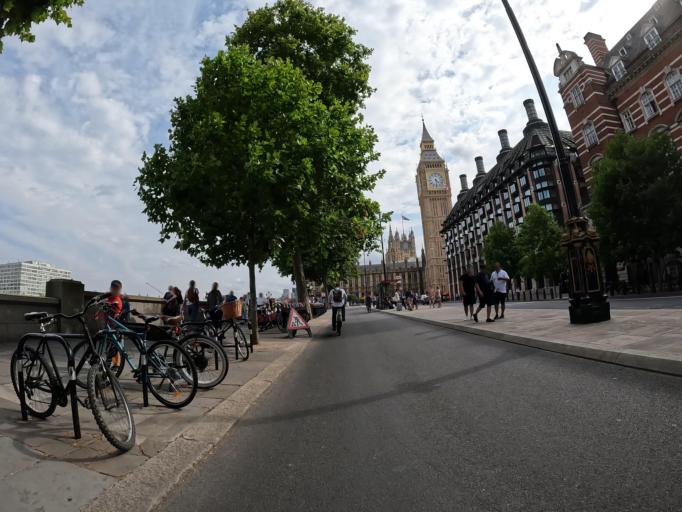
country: GB
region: England
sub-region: Greater London
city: Orpington
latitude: 51.3616
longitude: 0.0544
